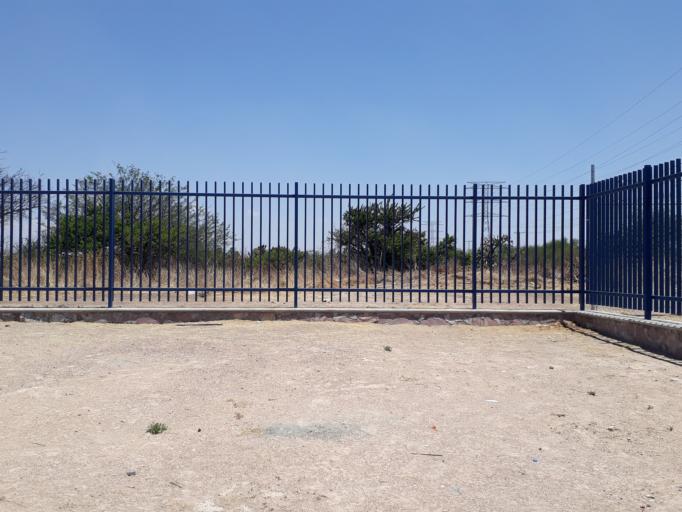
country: MX
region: Aguascalientes
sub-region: Aguascalientes
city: San Sebastian [Fraccionamiento]
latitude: 21.7941
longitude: -102.2878
